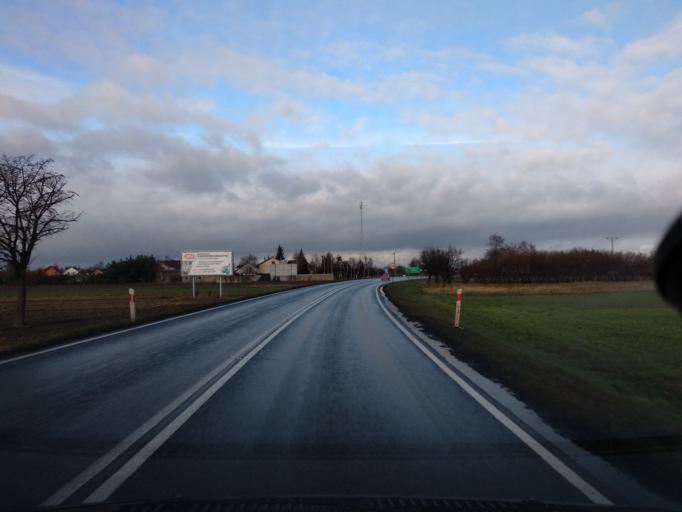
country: PL
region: Greater Poland Voivodeship
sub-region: Powiat koninski
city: Rychwal
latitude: 52.0711
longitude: 18.1581
